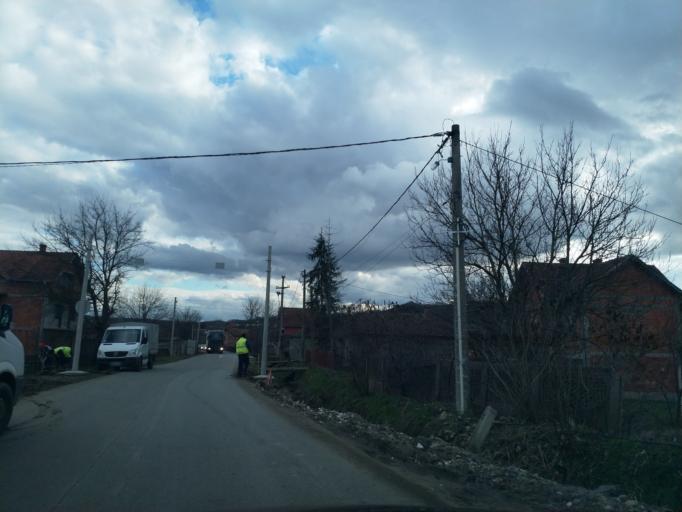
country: RS
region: Central Serbia
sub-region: Belgrade
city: Grocka
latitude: 44.5785
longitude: 20.7403
